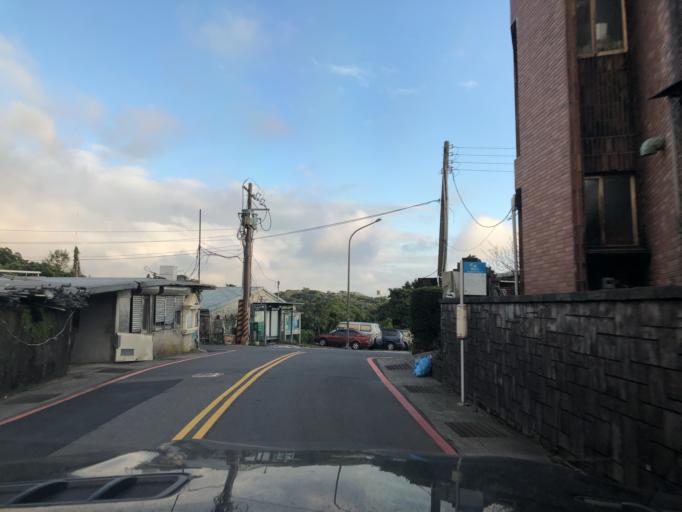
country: TW
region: Taipei
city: Taipei
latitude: 25.1467
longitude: 121.5587
